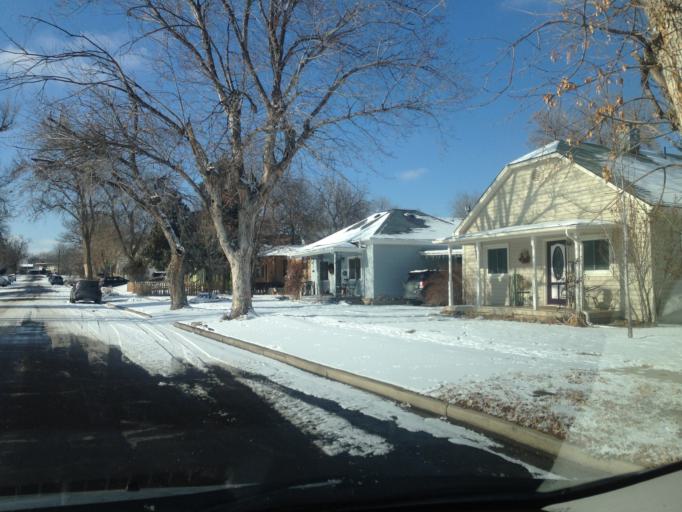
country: US
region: Colorado
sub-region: Boulder County
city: Lafayette
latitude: 39.9983
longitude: -105.0920
